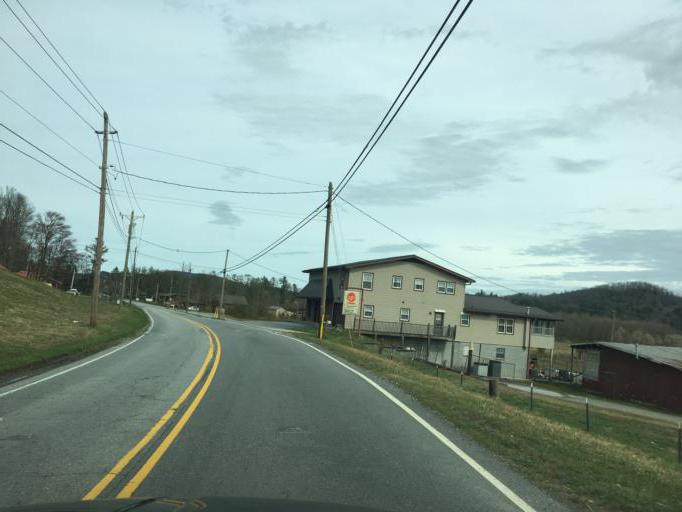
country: US
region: North Carolina
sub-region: Transylvania County
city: Brevard
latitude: 35.2466
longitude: -82.7128
